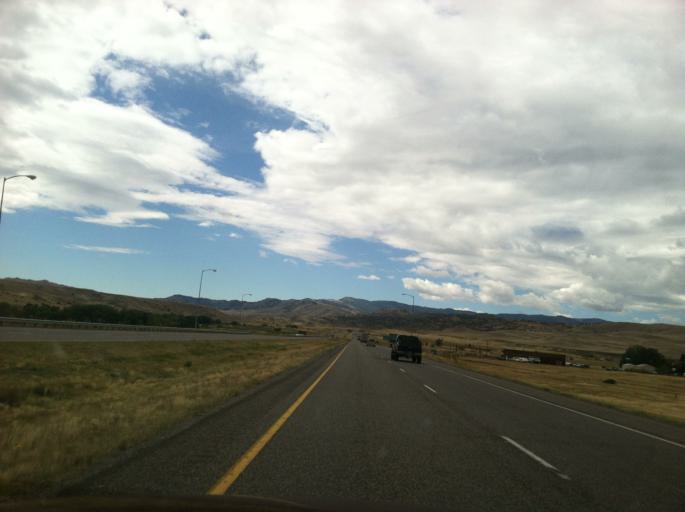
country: US
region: Montana
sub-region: Park County
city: Livingston
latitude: 45.6502
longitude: -110.6085
